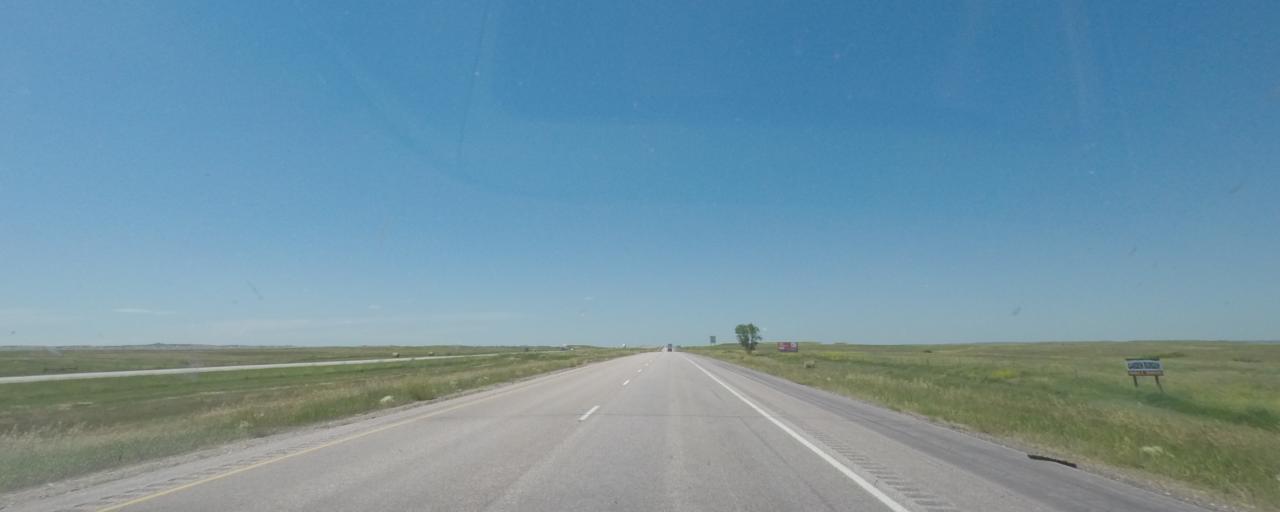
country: US
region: South Dakota
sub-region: Haakon County
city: Philip
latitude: 43.9422
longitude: -102.1572
